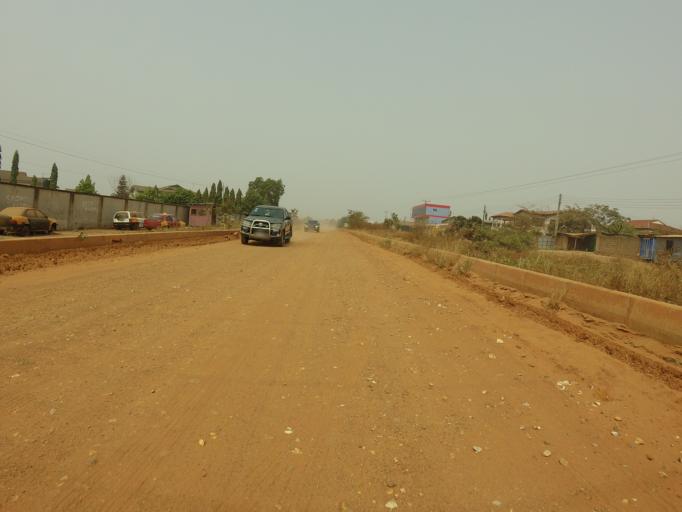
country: GH
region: Greater Accra
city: Teshi Old Town
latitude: 5.6282
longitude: -0.1243
